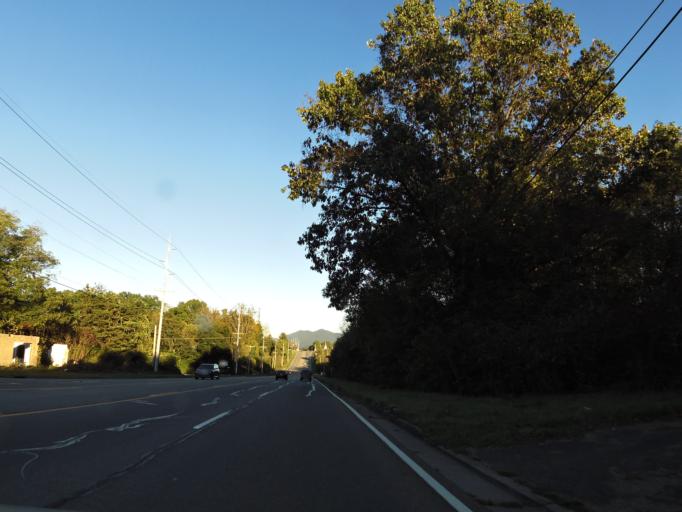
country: US
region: Tennessee
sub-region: Blount County
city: Eagleton Village
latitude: 35.7572
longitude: -83.9007
